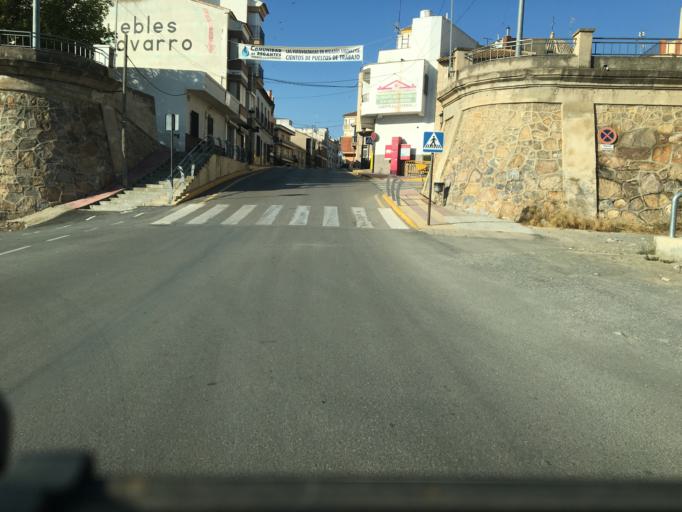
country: ES
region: Murcia
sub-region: Murcia
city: Puerto Lumbreras
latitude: 37.5605
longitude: -1.8099
